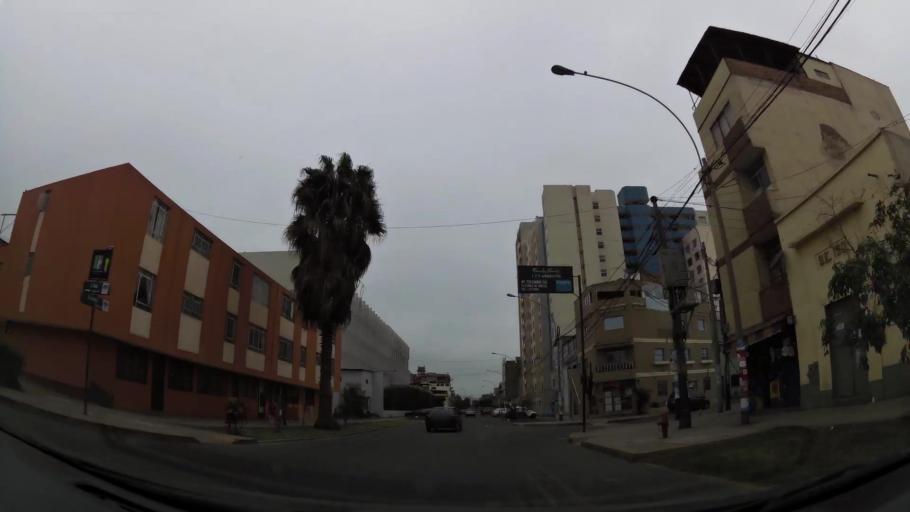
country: PE
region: Lima
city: Lima
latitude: -12.0693
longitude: -77.0528
